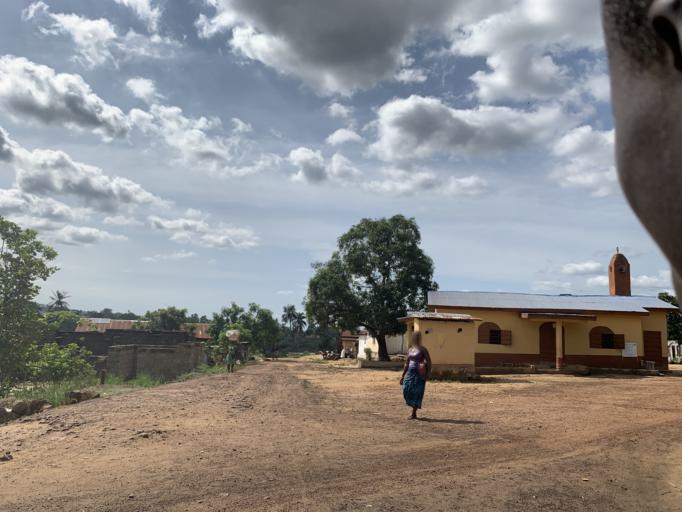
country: SL
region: Western Area
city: Waterloo
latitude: 8.3324
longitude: -13.0644
